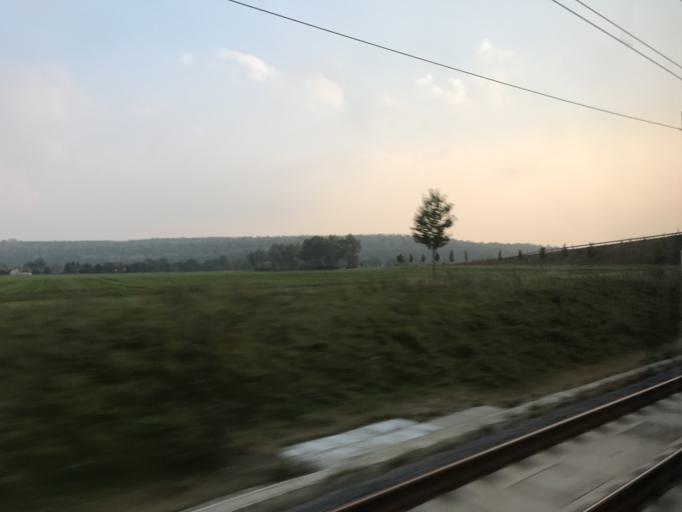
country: DE
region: Saxony-Anhalt
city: Bad Lauchstadt
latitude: 51.3558
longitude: 11.8285
